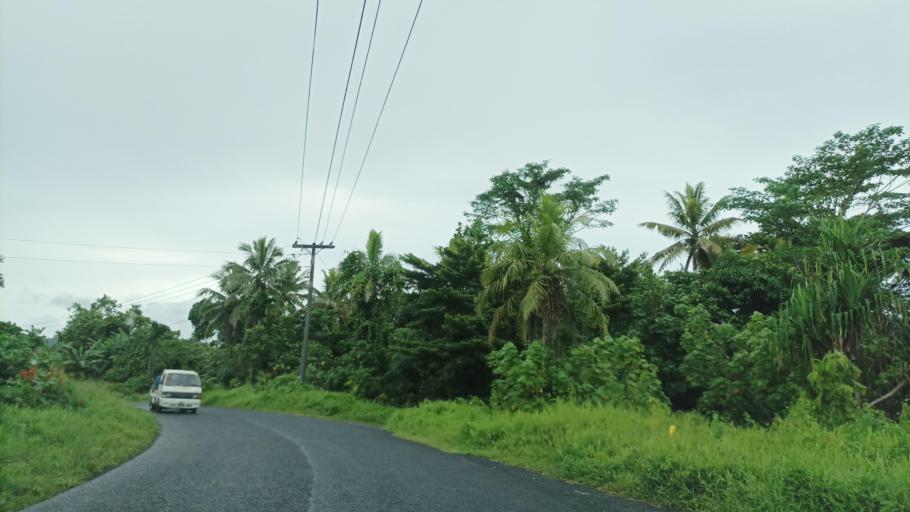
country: FM
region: Pohnpei
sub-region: Sokehs Municipality
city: Palikir - National Government Center
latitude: 6.8911
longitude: 158.1534
